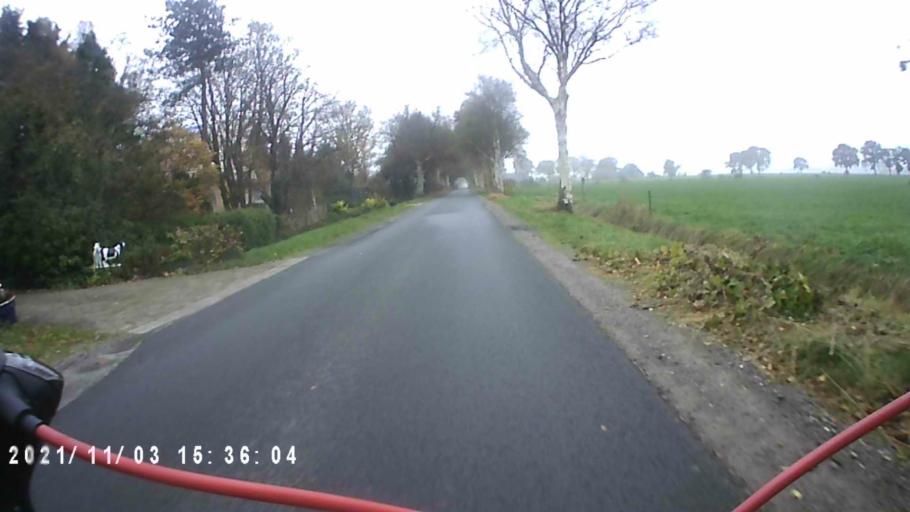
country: NL
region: Groningen
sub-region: Gemeente Leek
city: Leek
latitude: 53.1150
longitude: 6.3623
